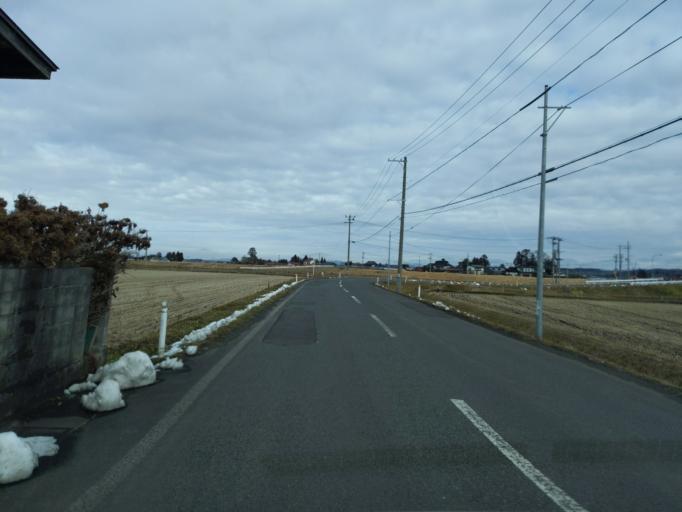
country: JP
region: Iwate
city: Mizusawa
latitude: 39.0808
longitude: 141.1653
